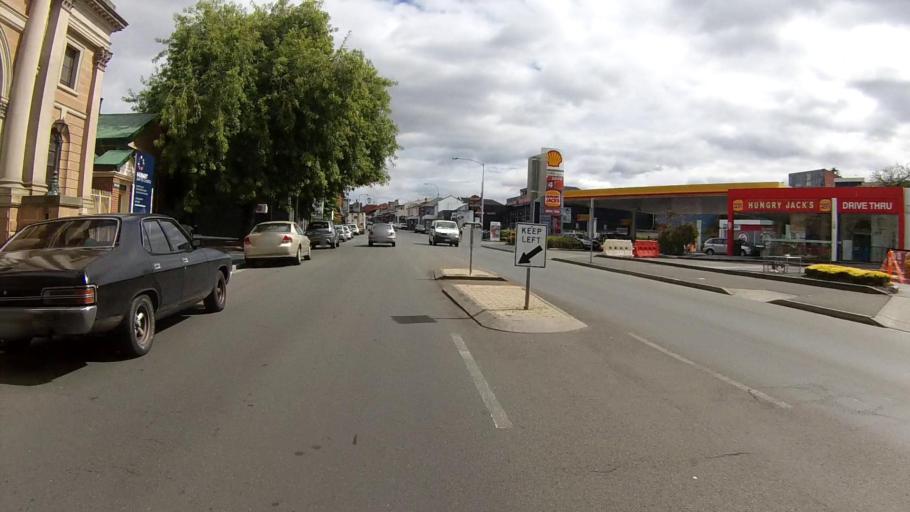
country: AU
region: Tasmania
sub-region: Hobart
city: Hobart
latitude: -42.8771
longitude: 147.3188
